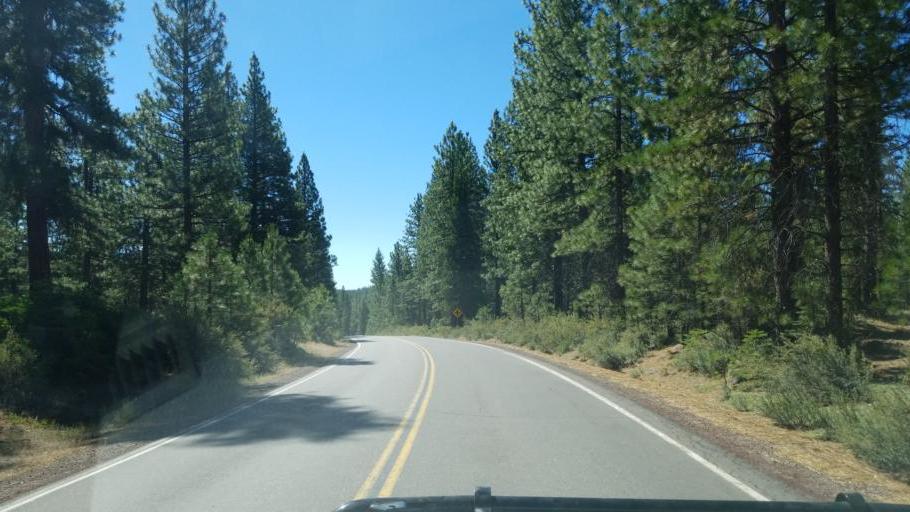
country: US
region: California
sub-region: Lassen County
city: Susanville
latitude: 40.4304
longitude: -120.7301
